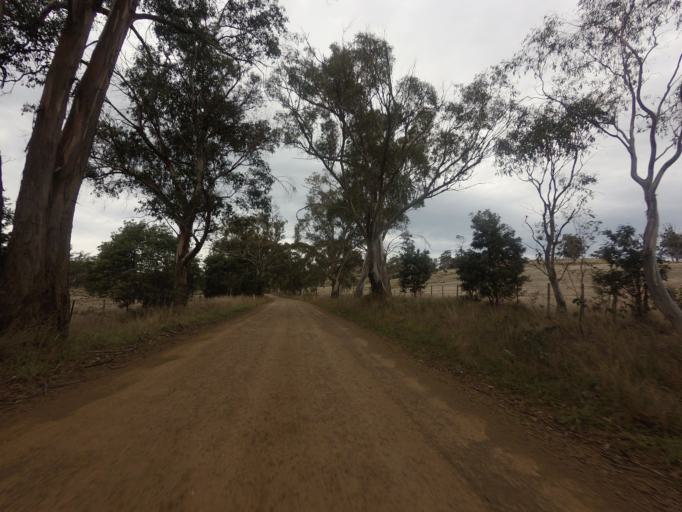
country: AU
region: Tasmania
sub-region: Derwent Valley
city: New Norfolk
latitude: -42.5626
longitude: 146.9252
